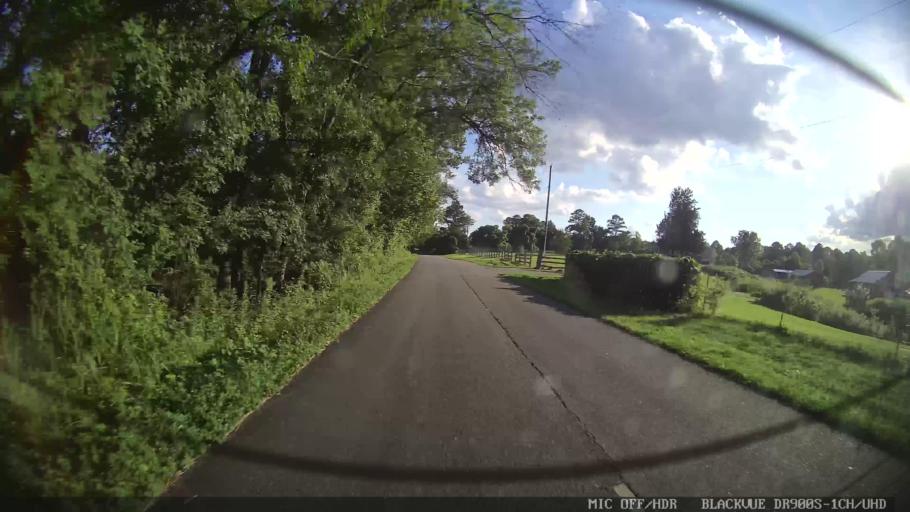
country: US
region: Georgia
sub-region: Bartow County
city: Rydal
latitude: 34.2913
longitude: -84.7409
